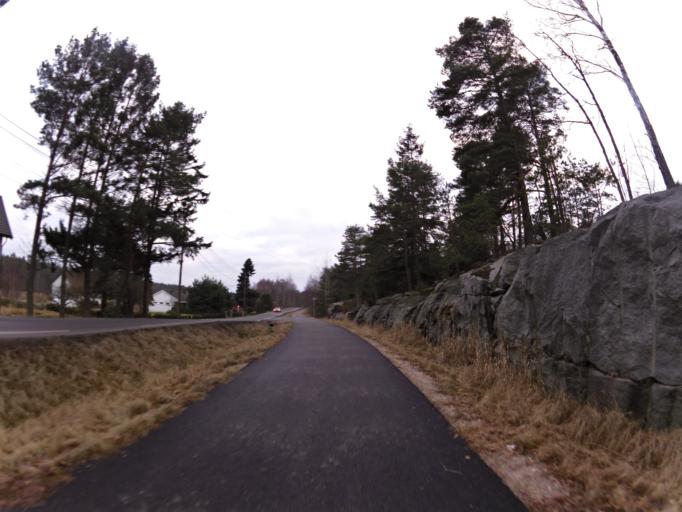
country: NO
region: Ostfold
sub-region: Fredrikstad
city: Fredrikstad
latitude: 59.1959
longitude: 10.8827
